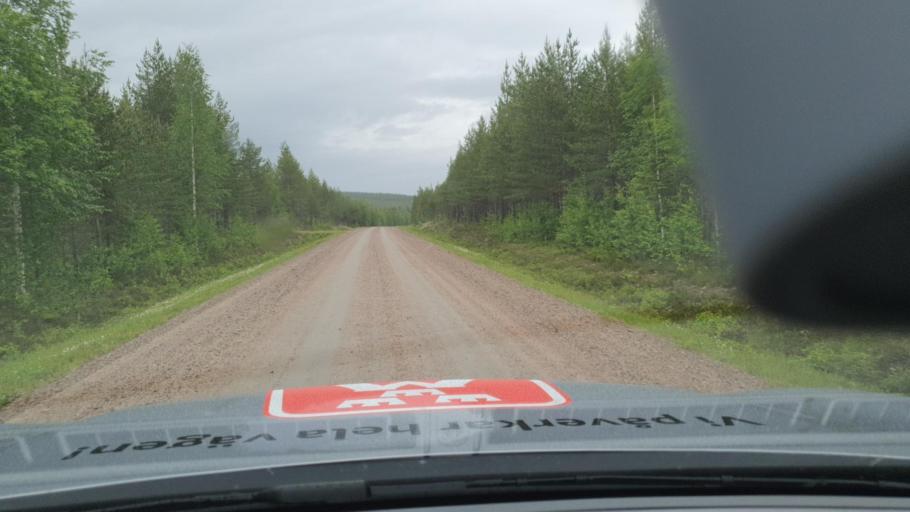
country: SE
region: Norrbotten
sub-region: Overkalix Kommun
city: OEverkalix
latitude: 66.5770
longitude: 22.7453
